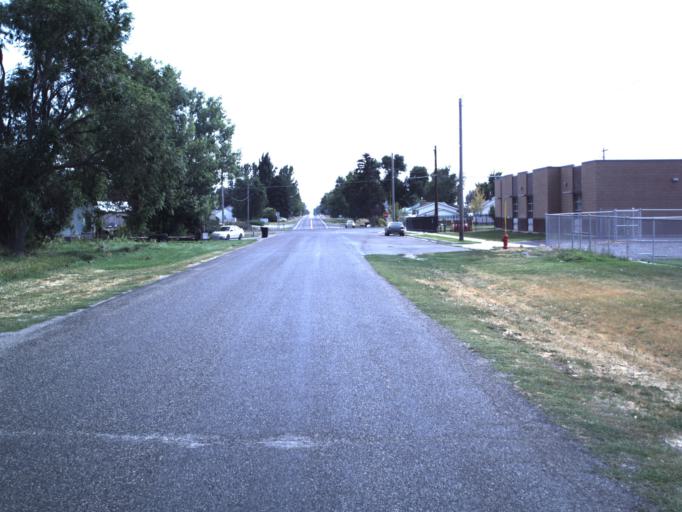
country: US
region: Utah
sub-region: Box Elder County
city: Garland
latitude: 41.8158
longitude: -112.1162
